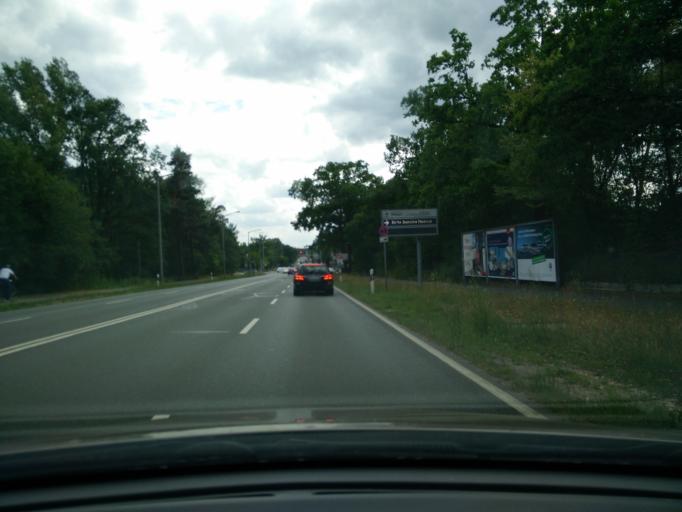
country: DE
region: Bavaria
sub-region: Regierungsbezirk Mittelfranken
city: Wendelstein
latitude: 49.4139
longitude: 11.1460
